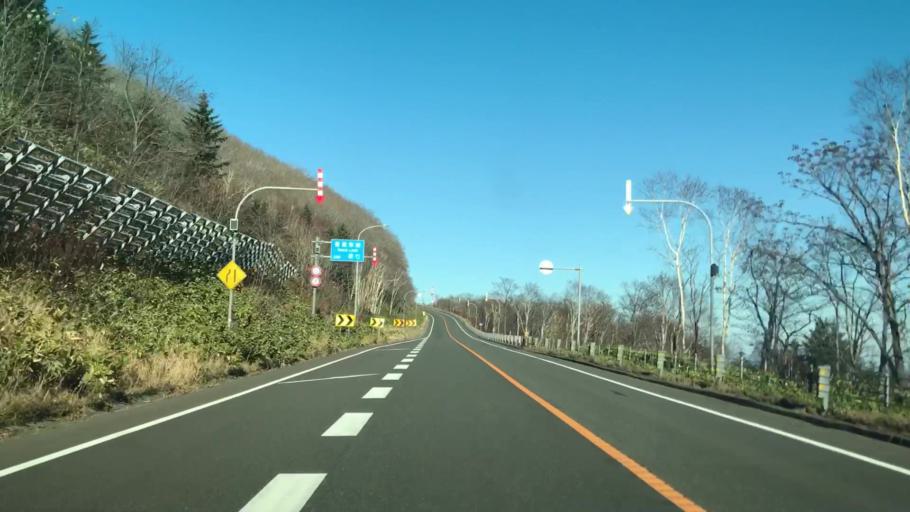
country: JP
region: Hokkaido
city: Otofuke
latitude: 42.9651
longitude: 142.7934
